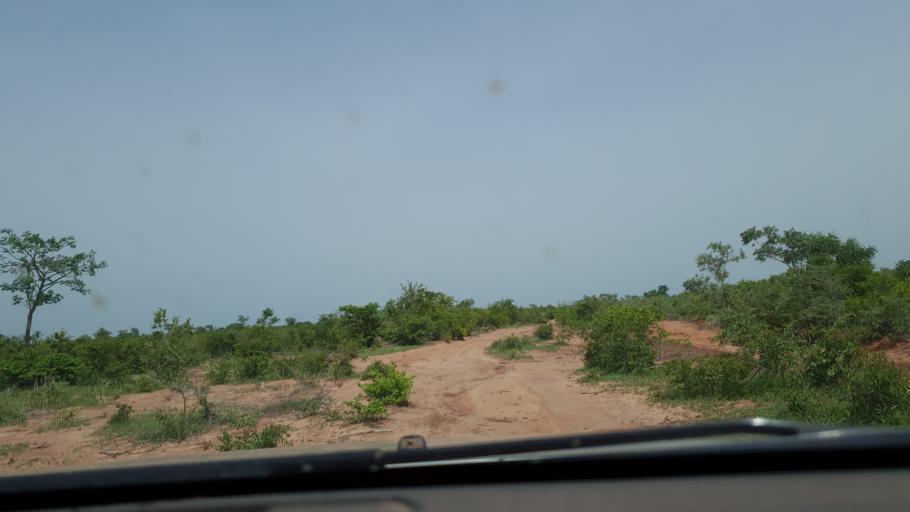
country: ML
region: Koulikoro
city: Koulikoro
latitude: 12.6653
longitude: -7.2240
